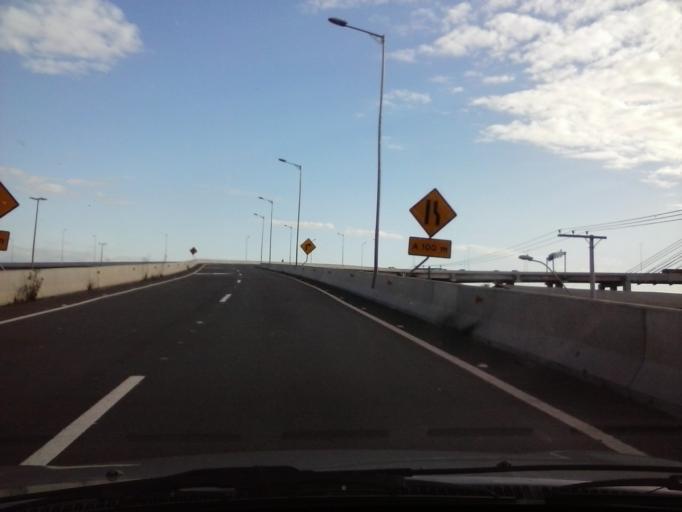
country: BR
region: Rio Grande do Sul
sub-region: Canoas
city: Canoas
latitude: -29.9721
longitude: -51.1963
